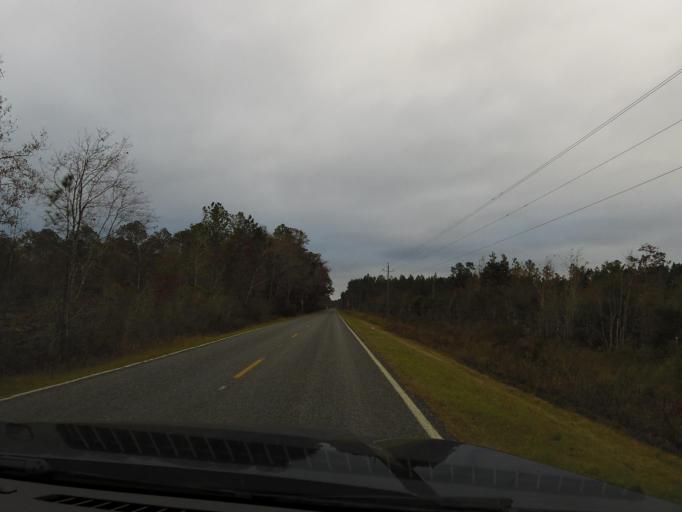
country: US
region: Georgia
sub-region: Charlton County
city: Folkston
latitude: 30.8758
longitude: -82.0483
